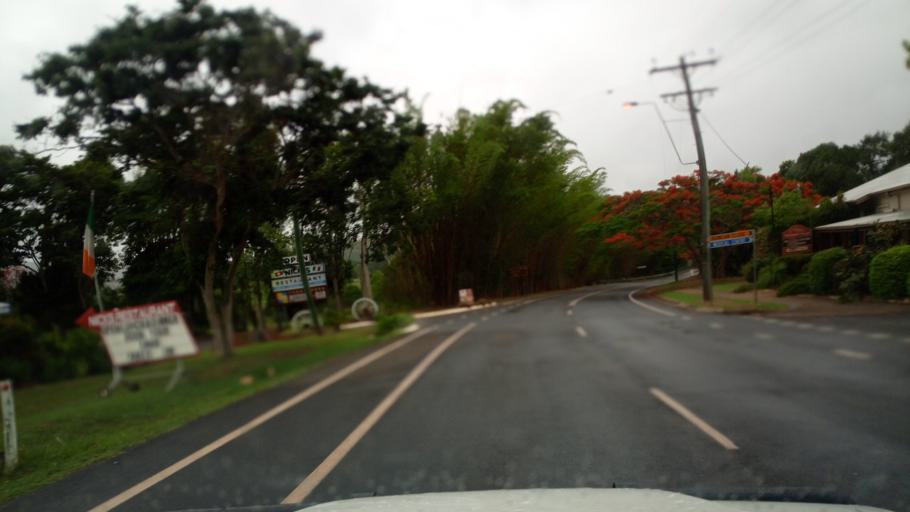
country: AU
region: Queensland
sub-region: Tablelands
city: Tolga
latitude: -17.2737
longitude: 145.5819
